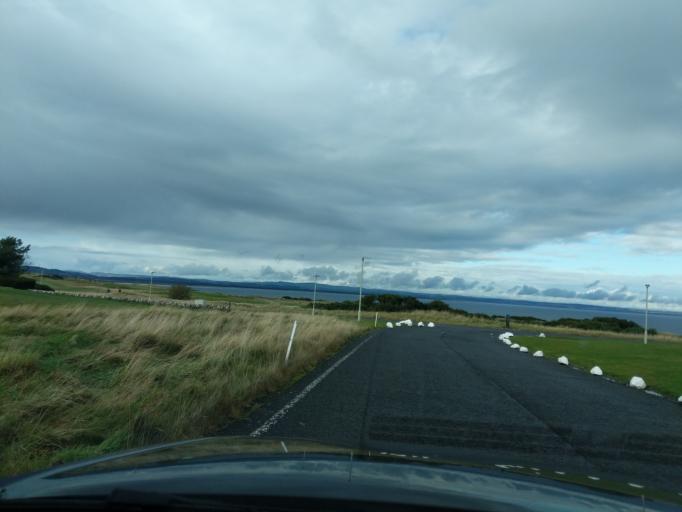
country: GB
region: Scotland
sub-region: Fife
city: Saint Andrews
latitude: 56.3207
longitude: -2.7336
